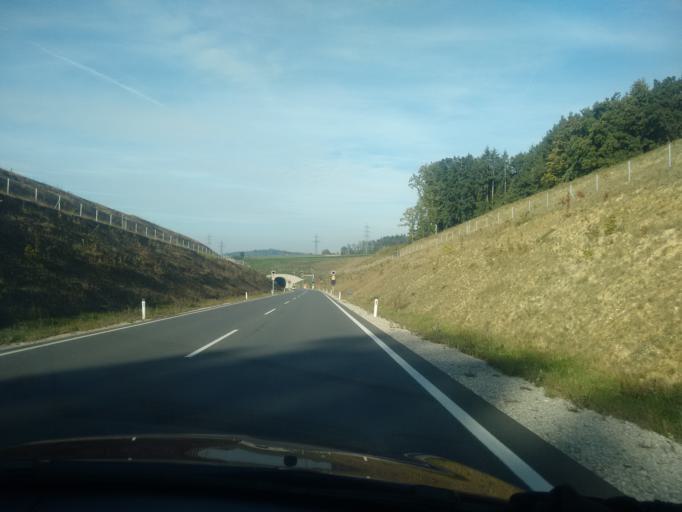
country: AT
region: Upper Austria
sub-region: Wels-Land
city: Lambach
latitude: 48.1015
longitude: 13.8738
